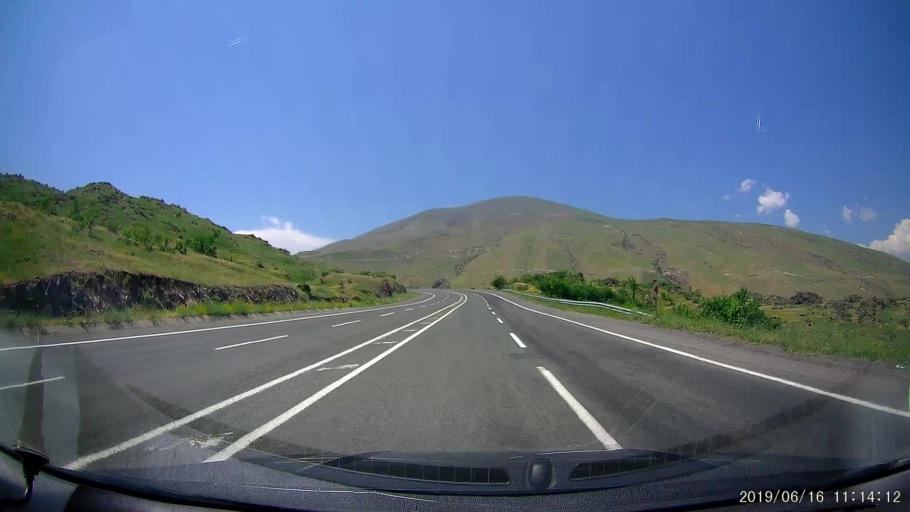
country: TR
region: Igdir
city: Igdir
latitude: 39.7821
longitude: 44.1443
